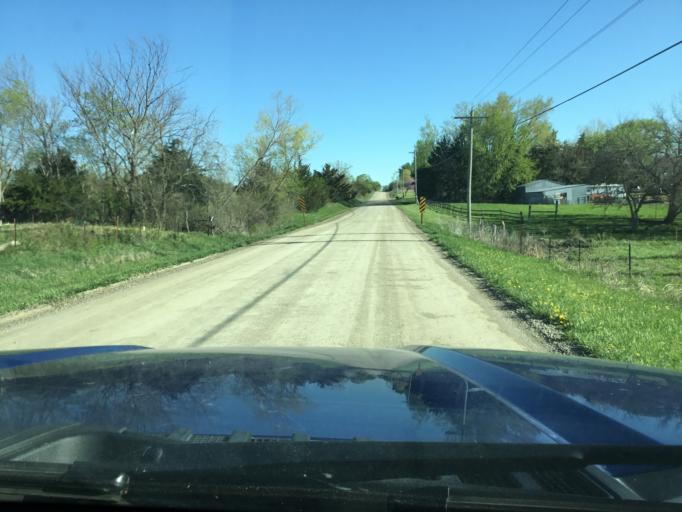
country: US
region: Kansas
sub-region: Douglas County
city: Lawrence
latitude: 38.9854
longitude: -95.3539
